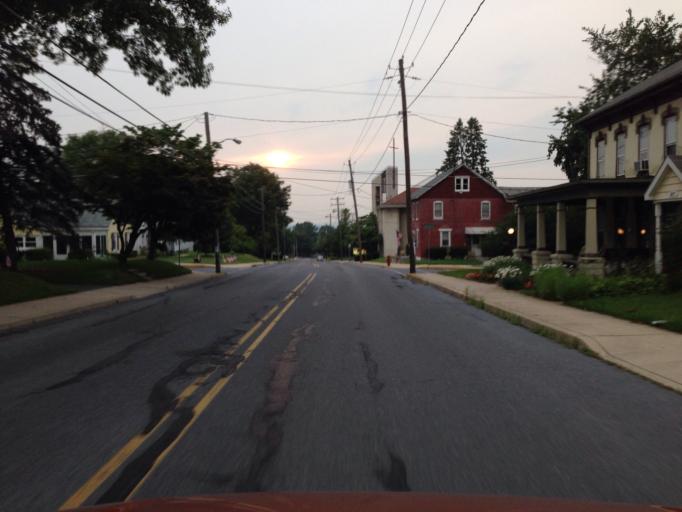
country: US
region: Pennsylvania
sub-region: Lancaster County
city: Akron
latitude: 40.1584
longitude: -76.2072
